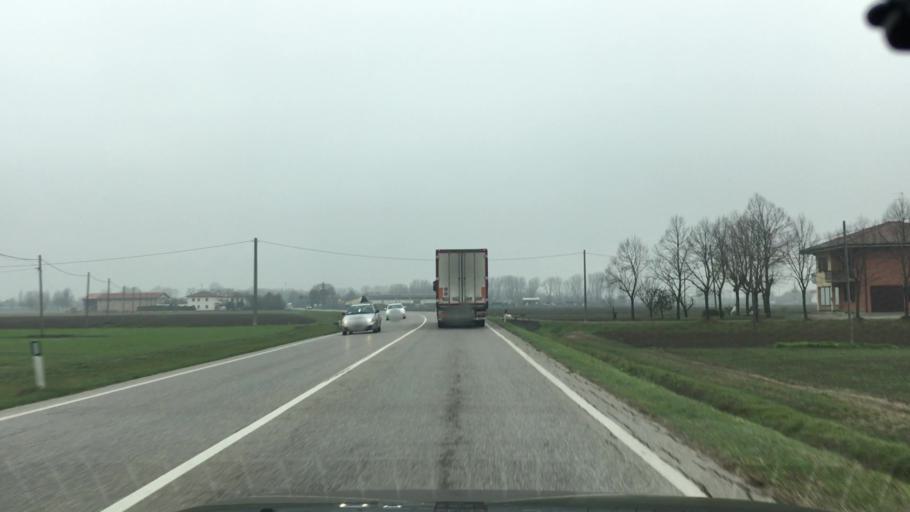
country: IT
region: Emilia-Romagna
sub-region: Provincia di Bologna
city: San Giovanni in Persiceto
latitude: 44.6259
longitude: 11.2173
